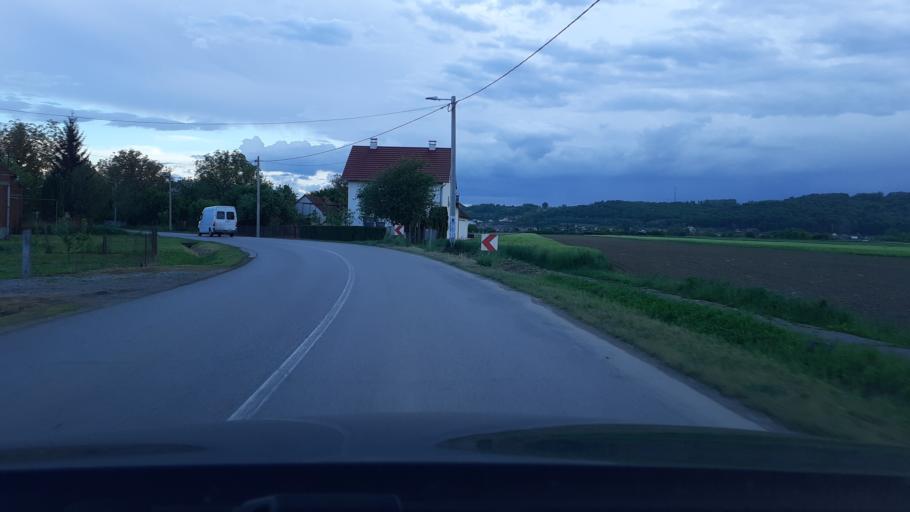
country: HR
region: Pozesko-Slavonska
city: Gradac
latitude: 45.3070
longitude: 17.8081
